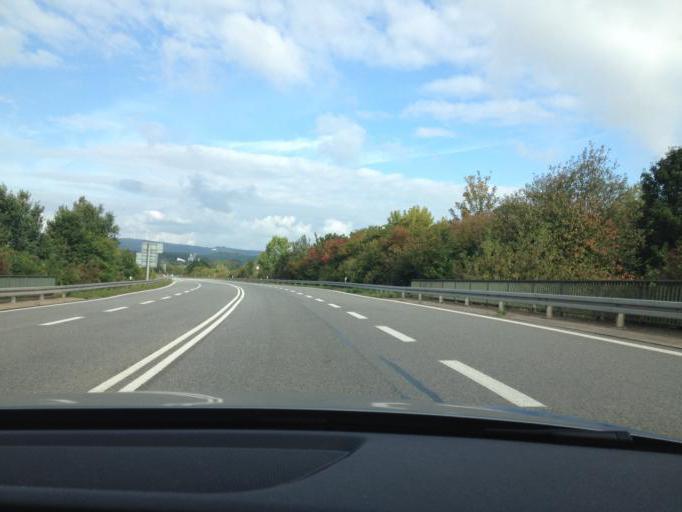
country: DE
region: Saarland
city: Sankt Wendel
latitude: 49.4720
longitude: 7.1488
